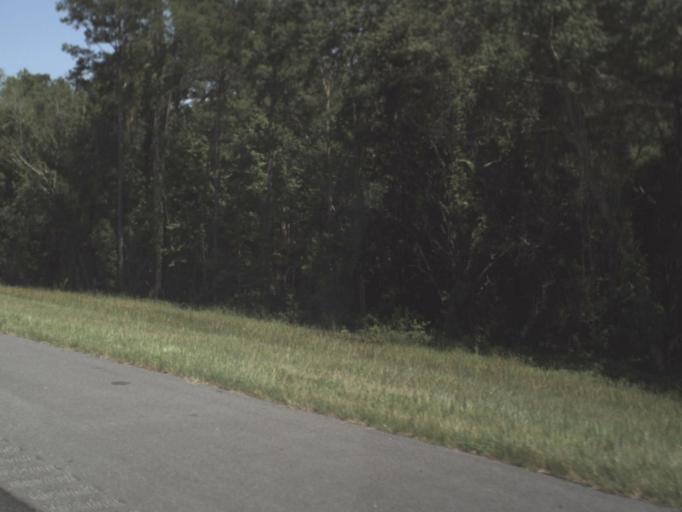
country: US
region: Florida
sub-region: Madison County
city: Madison
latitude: 30.3611
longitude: -83.2117
